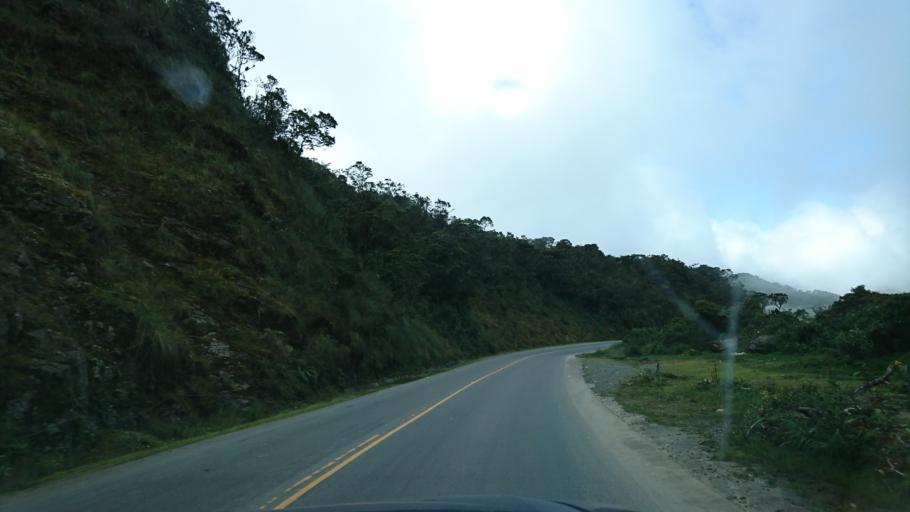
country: BO
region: La Paz
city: Coroico
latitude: -16.2866
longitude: -67.8525
